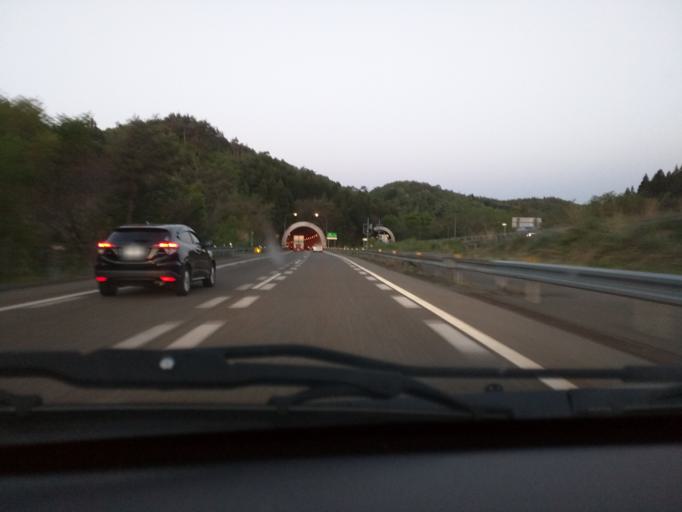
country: JP
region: Niigata
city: Kashiwazaki
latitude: 37.3384
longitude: 138.5348
